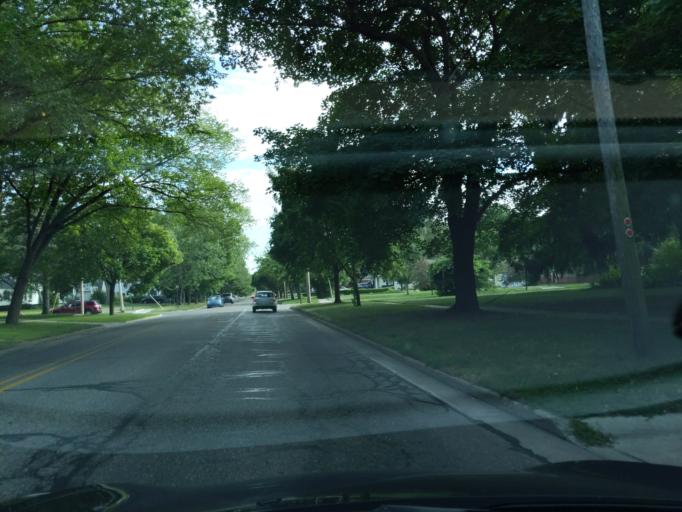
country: US
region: Michigan
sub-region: Midland County
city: Midland
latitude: 43.6402
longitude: -84.2269
